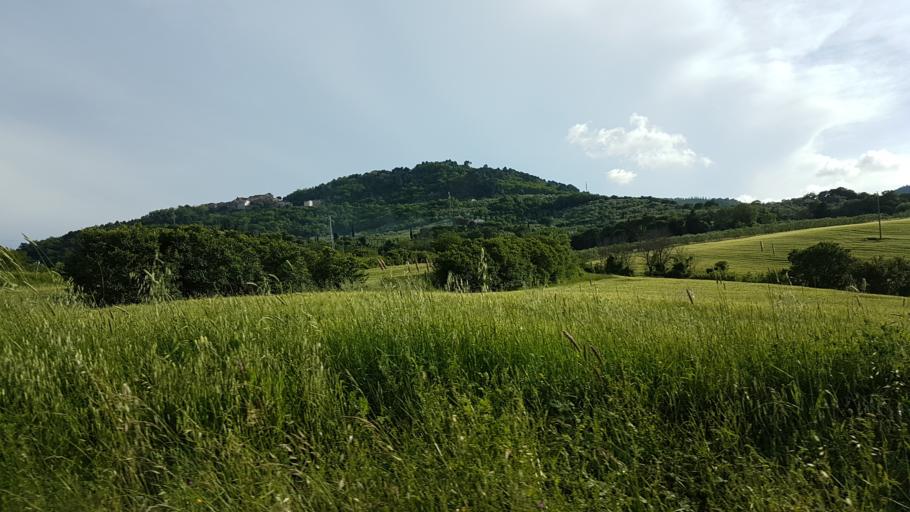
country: IT
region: Tuscany
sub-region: Province of Pisa
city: Chianni
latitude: 43.5058
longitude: 10.6408
